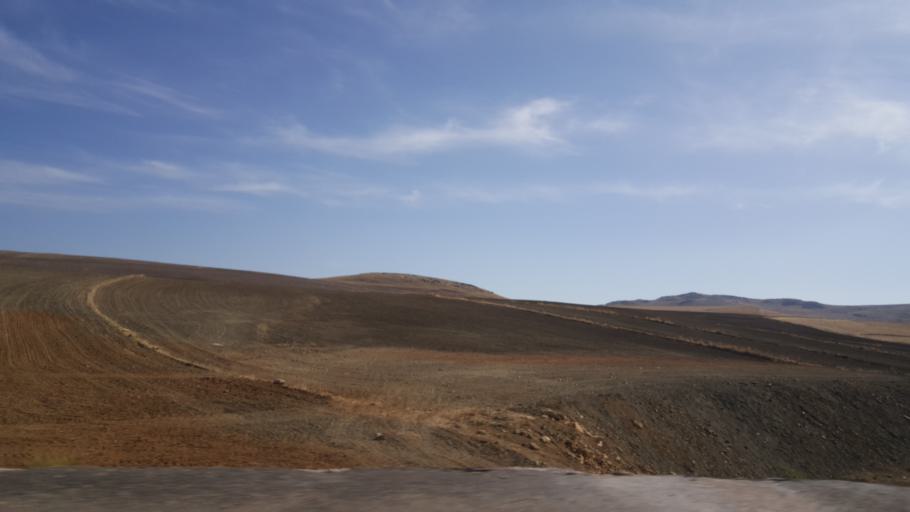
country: TR
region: Ankara
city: Yenice
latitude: 39.3661
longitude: 32.7131
